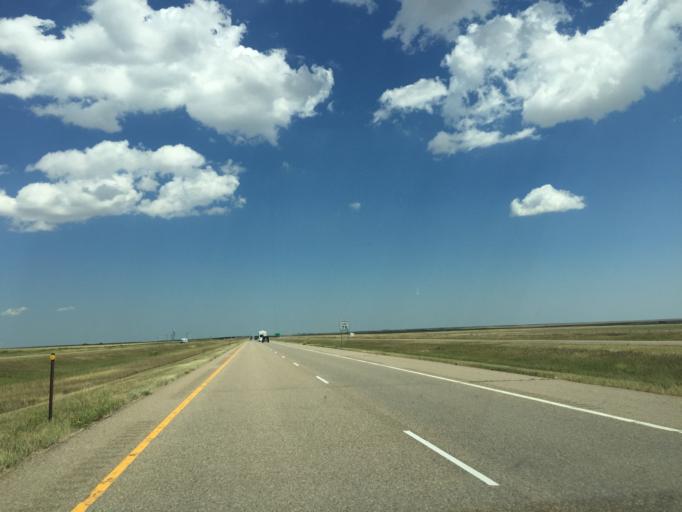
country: US
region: Colorado
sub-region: Lincoln County
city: Hugo
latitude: 39.2767
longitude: -103.4776
